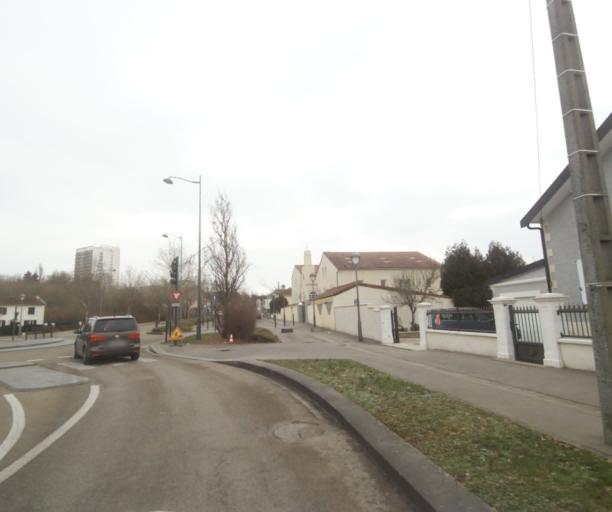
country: FR
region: Champagne-Ardenne
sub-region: Departement de la Haute-Marne
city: Bettancourt-la-Ferree
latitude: 48.6364
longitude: 4.9761
